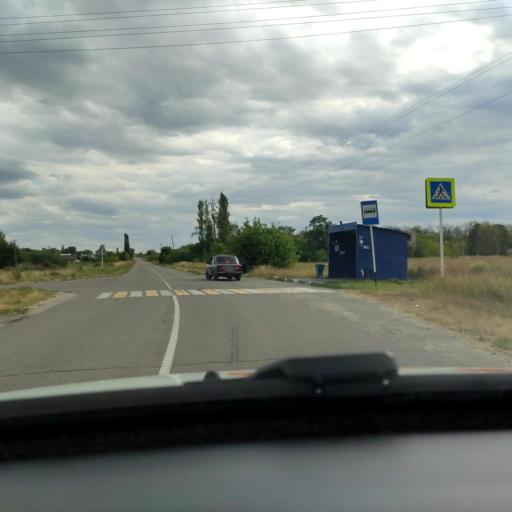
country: RU
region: Voronezj
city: Orlovo
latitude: 51.6615
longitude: 39.5714
